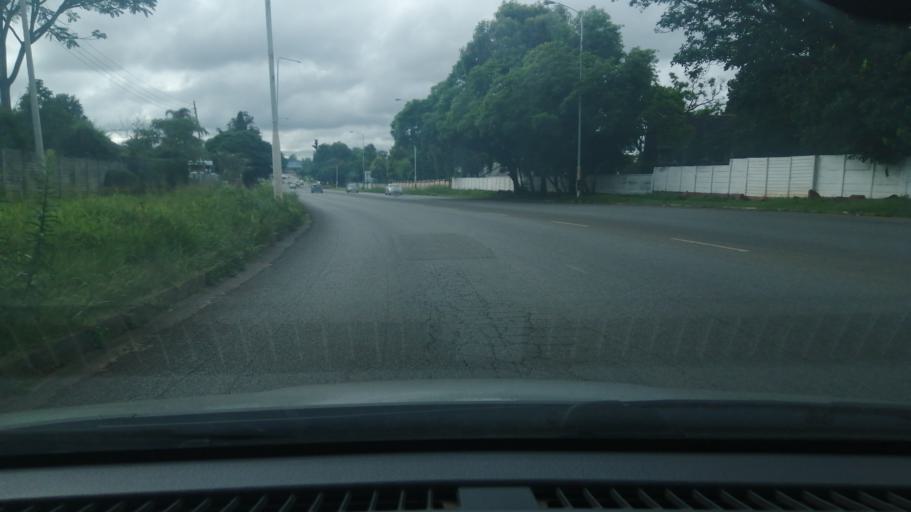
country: ZW
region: Harare
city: Harare
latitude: -17.7879
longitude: 31.0411
